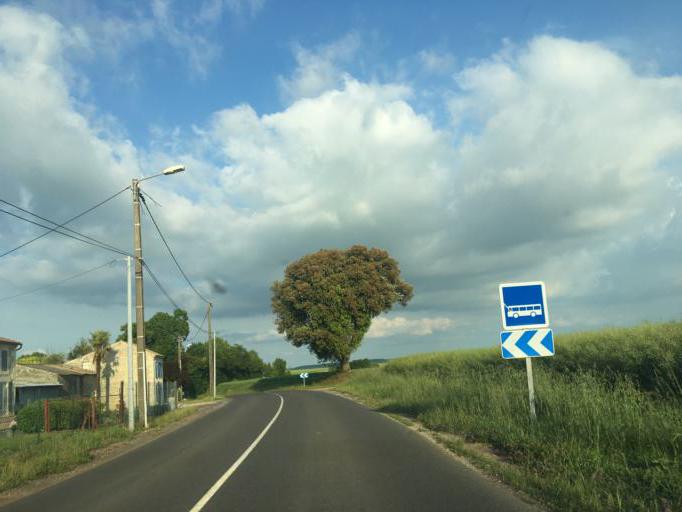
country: FR
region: Poitou-Charentes
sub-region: Departement des Deux-Sevres
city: Mauze-sur-le-Mignon
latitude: 46.0859
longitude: -0.5889
